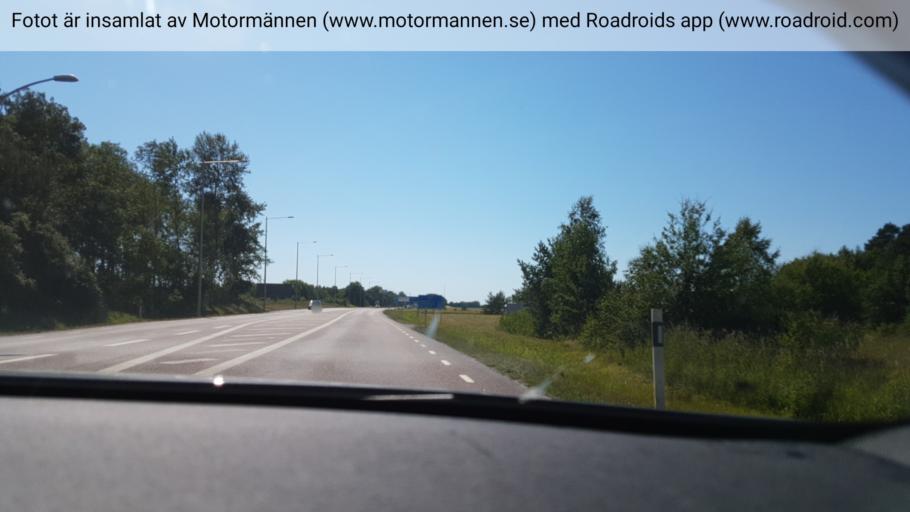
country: SE
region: Vaestra Goetaland
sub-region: Gotene Kommun
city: Goetene
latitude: 58.5381
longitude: 13.5121
